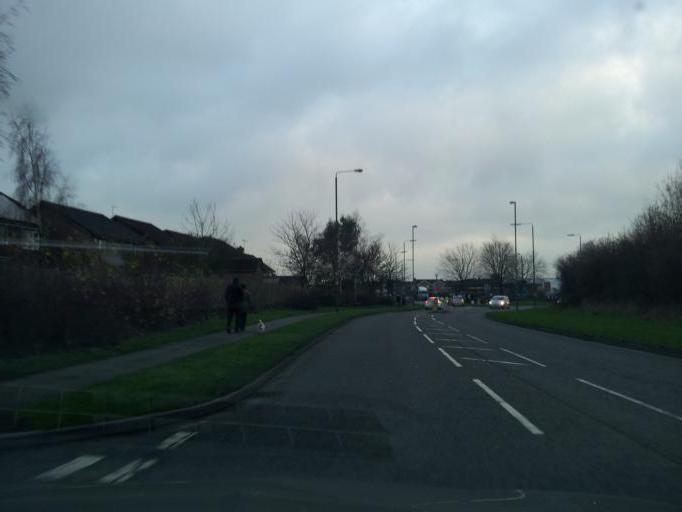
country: GB
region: England
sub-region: Derbyshire
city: Etwall
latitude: 52.8729
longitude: -1.6280
